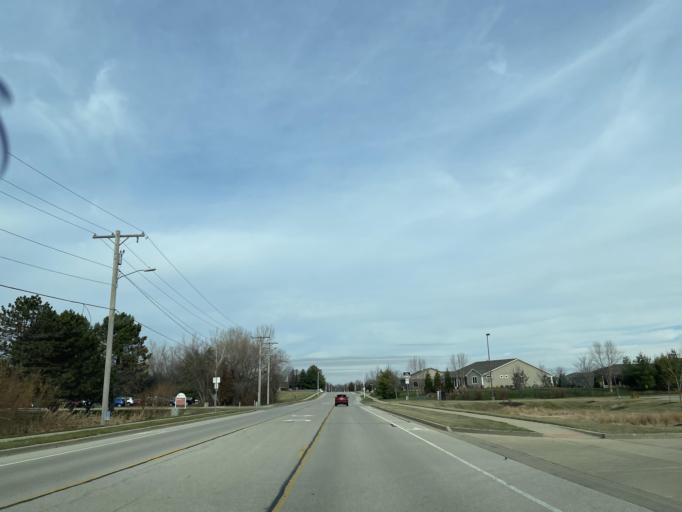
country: US
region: Illinois
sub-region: Sangamon County
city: Jerome
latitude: 39.7718
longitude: -89.7298
